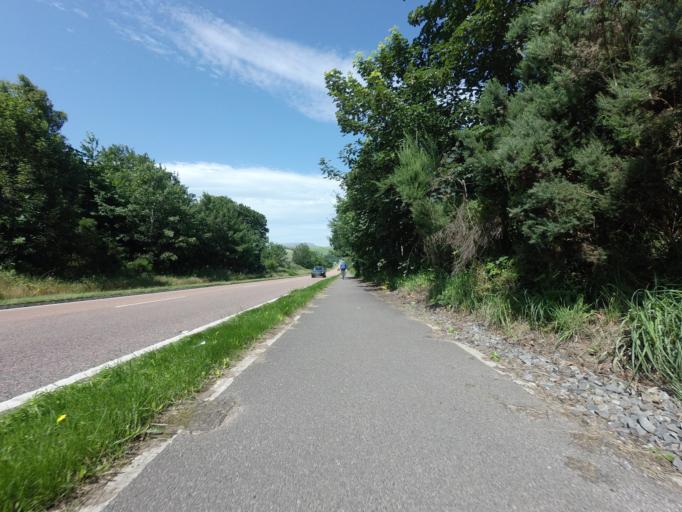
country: GB
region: Scotland
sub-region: Highland
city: Conon Bridge
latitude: 57.5696
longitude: -4.4267
